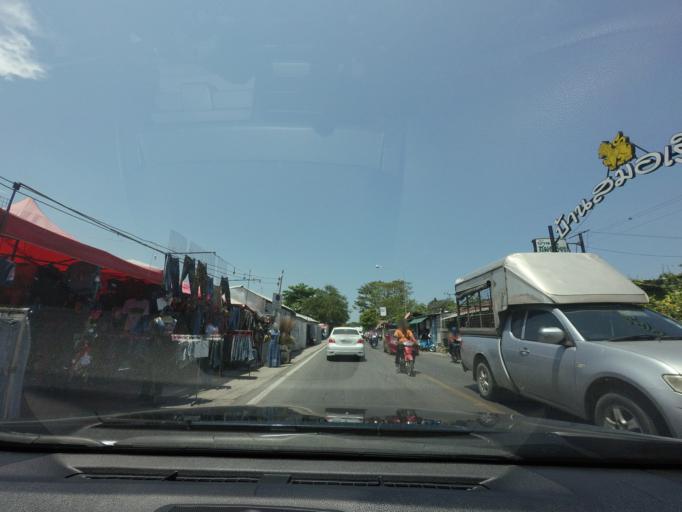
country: TH
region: Prachuap Khiri Khan
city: Hua Hin
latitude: 12.5625
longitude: 99.9560
